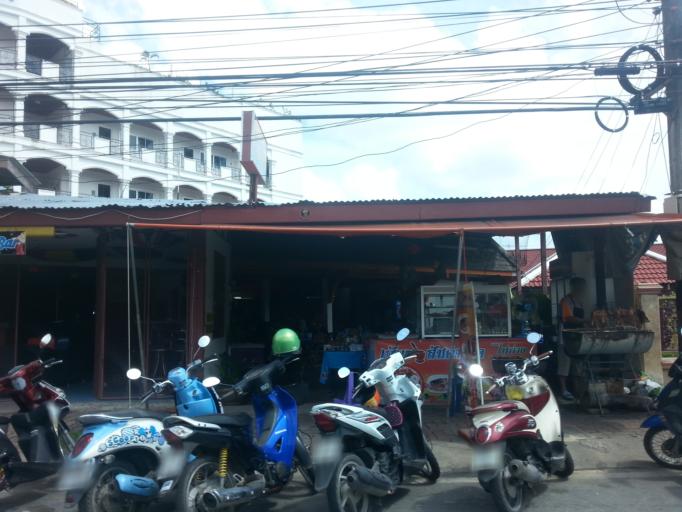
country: TH
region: Phuket
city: Kathu
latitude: 7.9121
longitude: 98.3333
